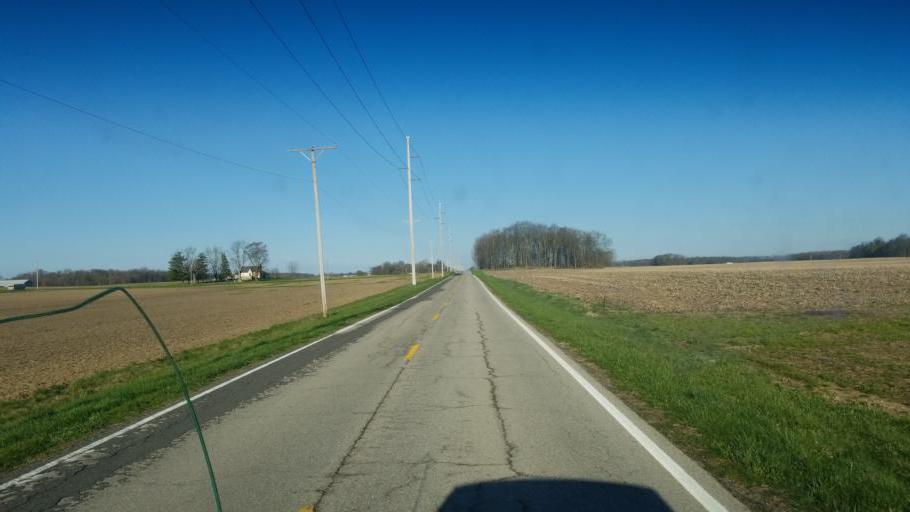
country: US
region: Ohio
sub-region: Union County
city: Richwood
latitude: 40.4568
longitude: -83.3170
